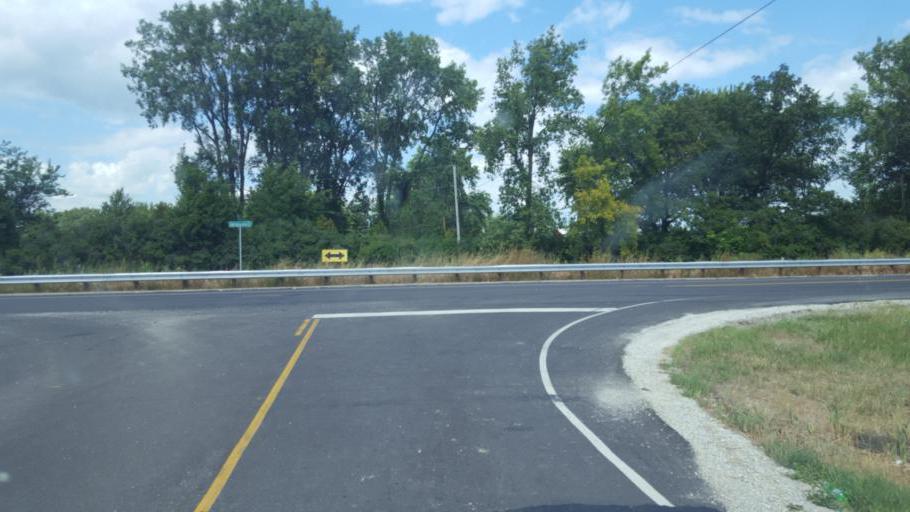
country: US
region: Ohio
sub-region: Lucas County
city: Curtice
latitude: 41.6385
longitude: -83.2795
